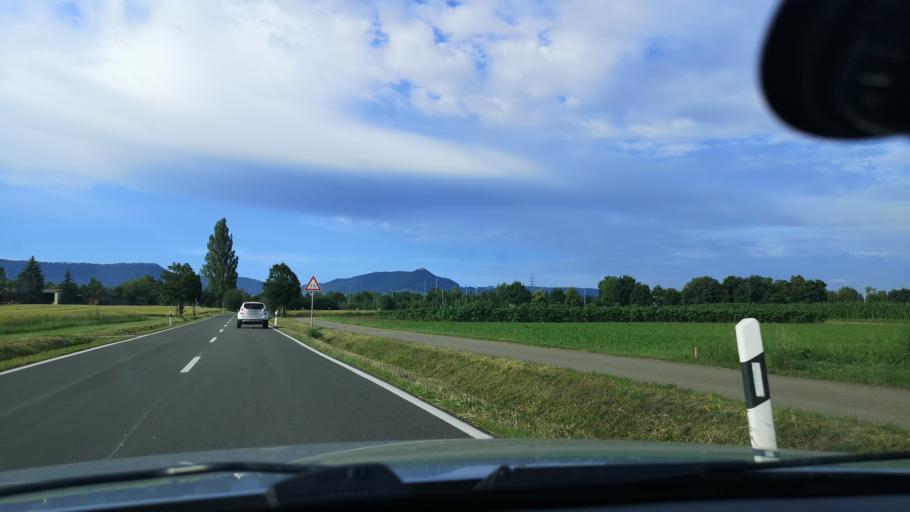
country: DE
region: Baden-Wuerttemberg
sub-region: Regierungsbezirk Stuttgart
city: Ohmden
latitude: 48.6426
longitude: 9.4961
